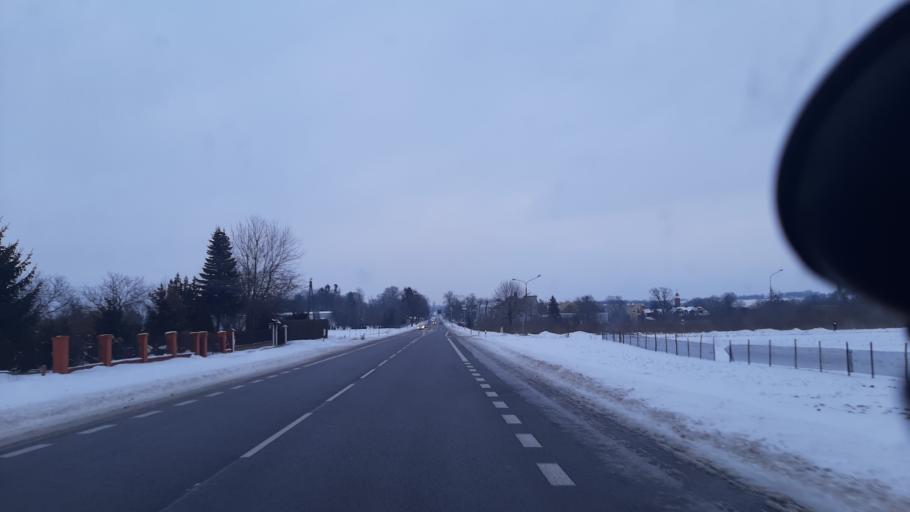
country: PL
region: Lublin Voivodeship
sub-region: Powiat pulawski
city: Markuszow
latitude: 51.3664
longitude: 22.2907
